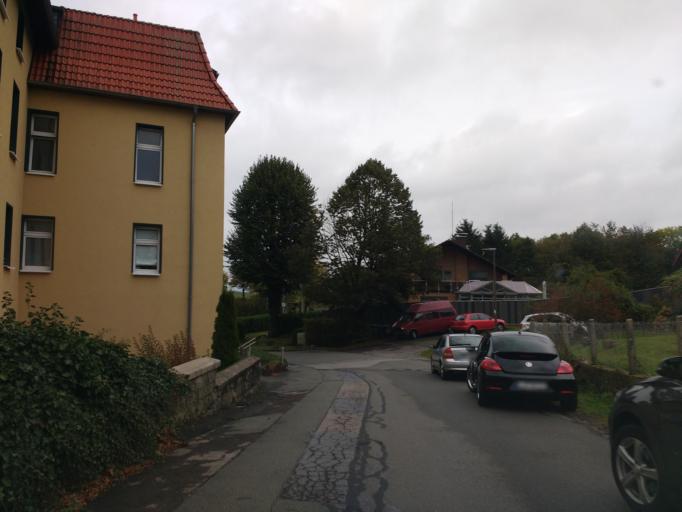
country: DE
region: North Rhine-Westphalia
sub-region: Regierungsbezirk Detmold
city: Horn
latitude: 51.8769
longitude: 8.9094
